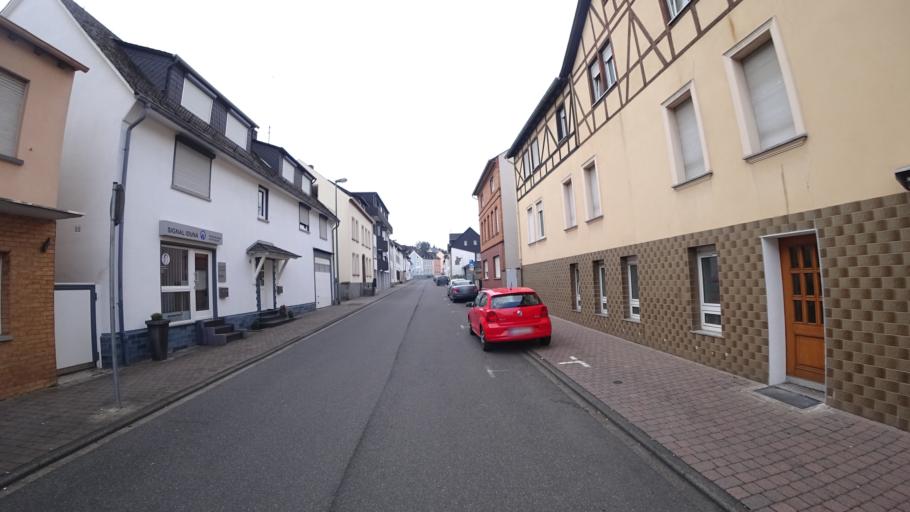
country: DE
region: Rheinland-Pfalz
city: Hohr-Grenzhausen
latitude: 50.4323
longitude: 7.6693
